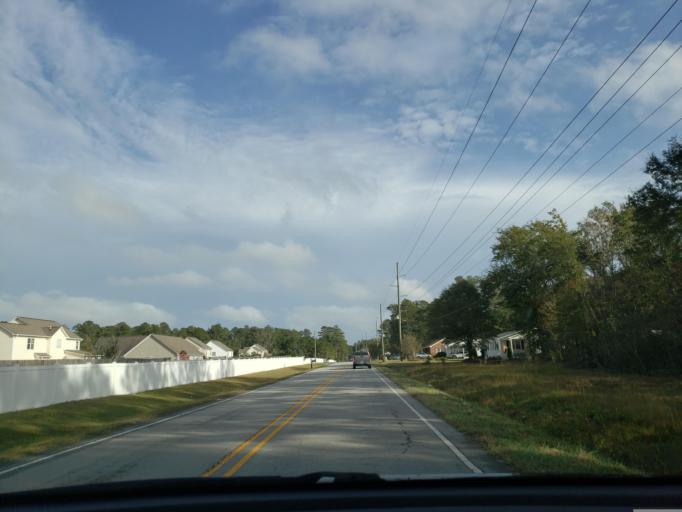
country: US
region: North Carolina
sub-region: Onslow County
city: Jacksonville
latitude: 34.6874
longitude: -77.5329
